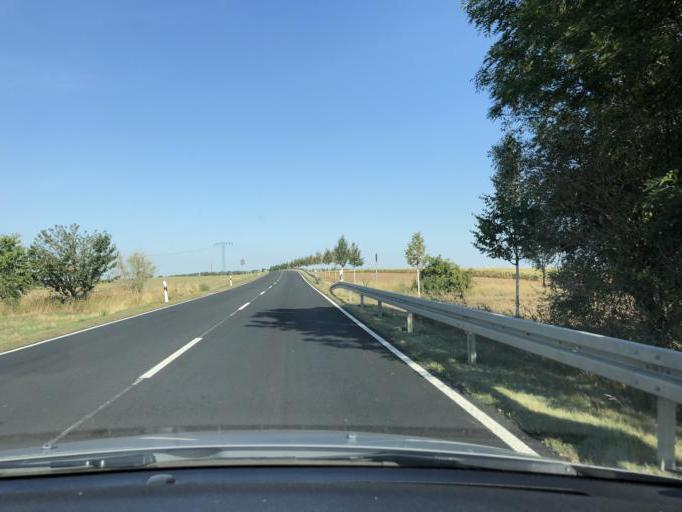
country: DE
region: Saxony-Anhalt
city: Braunsbedra
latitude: 51.2698
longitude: 11.9002
